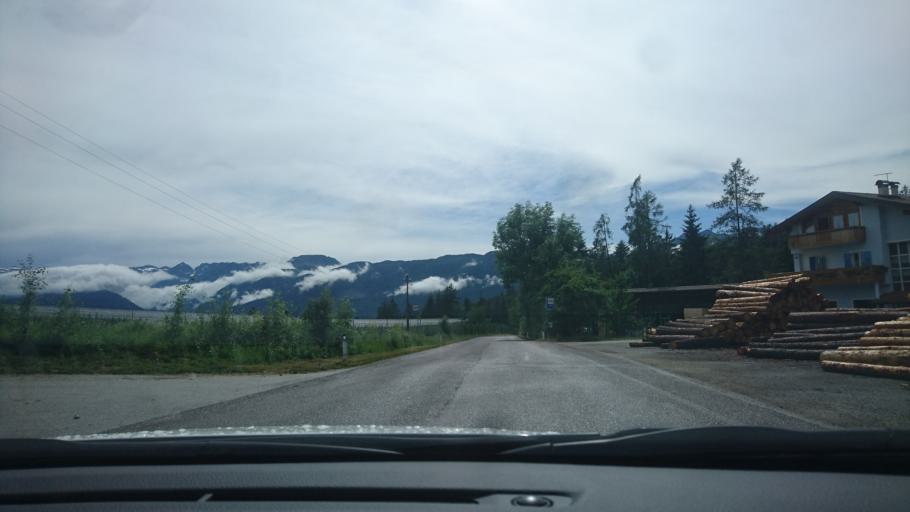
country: IT
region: Trentino-Alto Adige
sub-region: Provincia di Trento
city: Dambel
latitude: 46.3847
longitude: 11.0958
